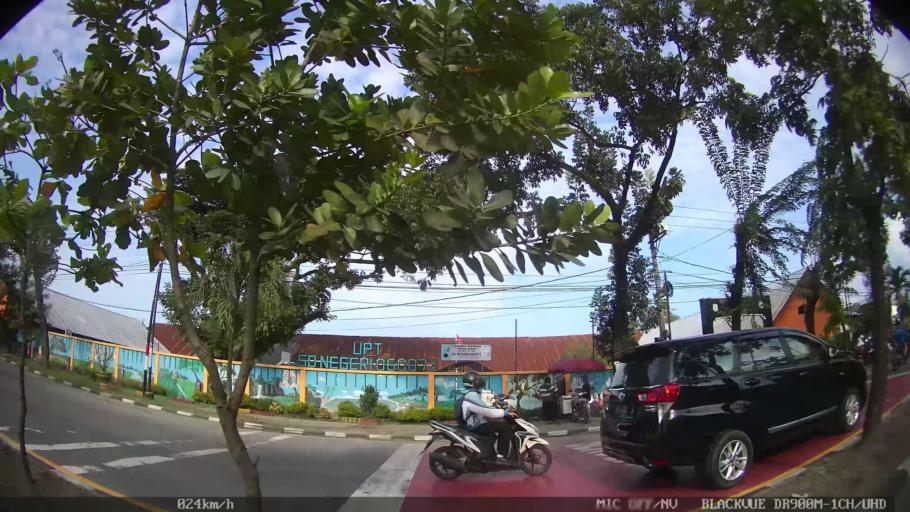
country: ID
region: North Sumatra
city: Medan
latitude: 3.6352
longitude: 98.6815
